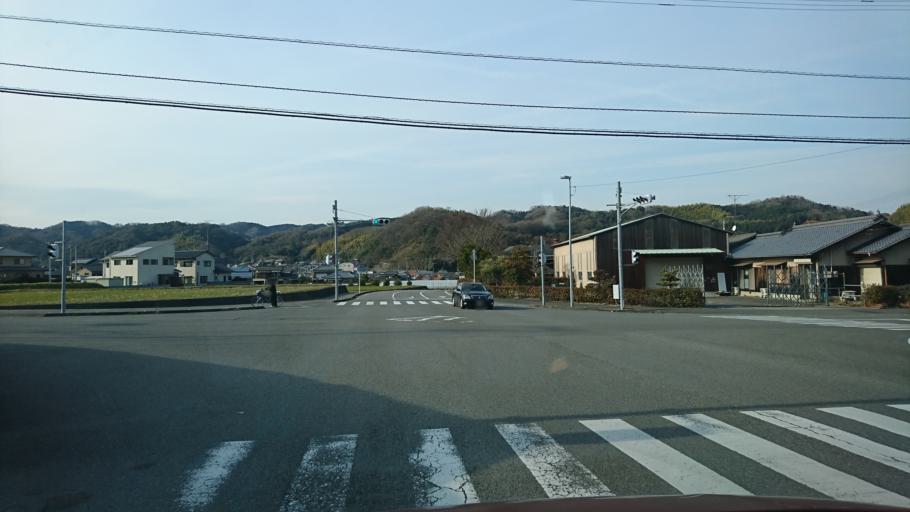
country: JP
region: Ehime
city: Hojo
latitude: 34.0244
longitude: 132.9613
